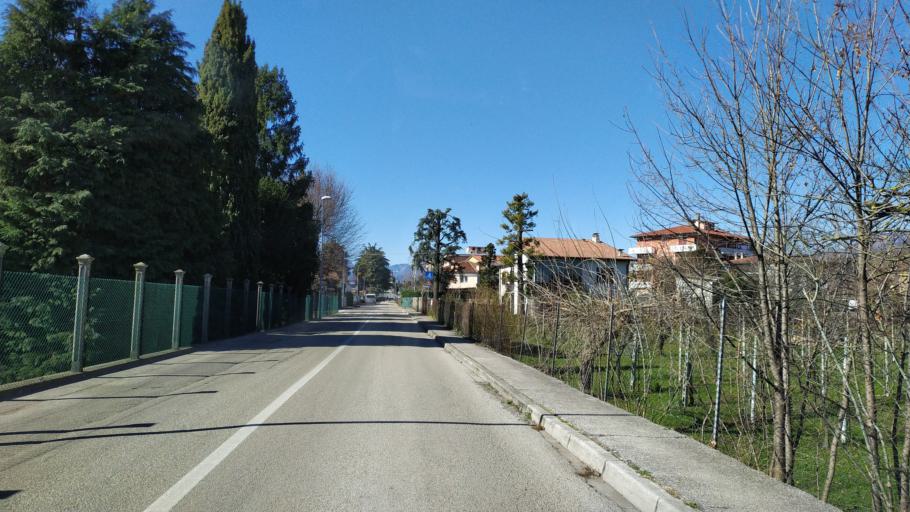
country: IT
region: Veneto
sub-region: Provincia di Vicenza
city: Breganze
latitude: 45.7057
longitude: 11.5684
